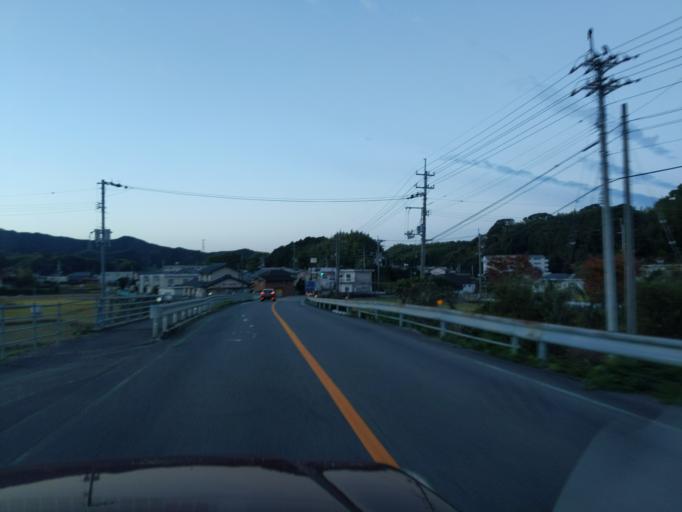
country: JP
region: Tokushima
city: Anan
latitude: 33.8436
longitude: 134.6246
